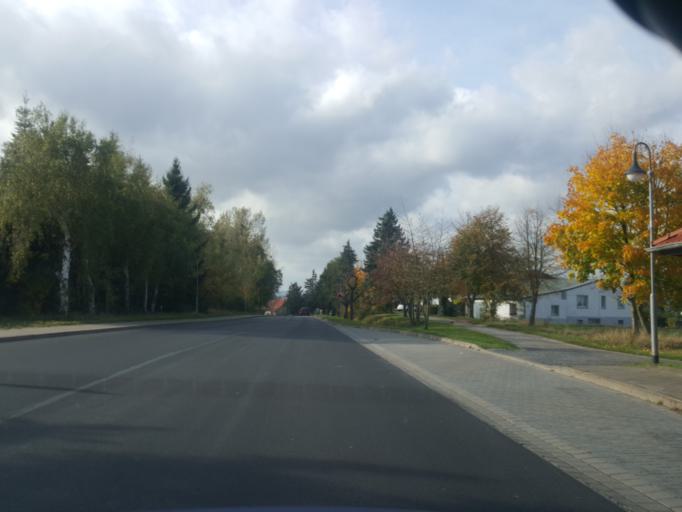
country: DE
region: Saxony-Anhalt
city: Blankenheim
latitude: 51.5061
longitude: 11.4382
